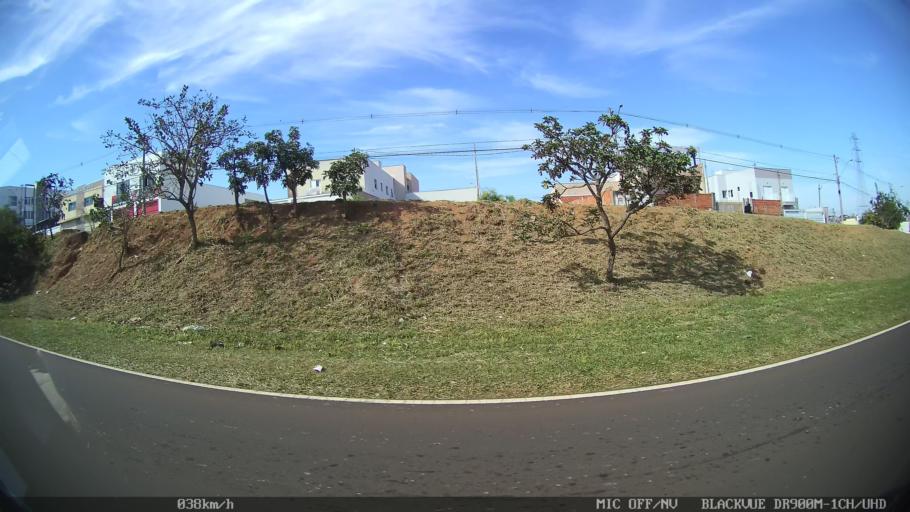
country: BR
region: Sao Paulo
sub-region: Franca
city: Franca
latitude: -20.5140
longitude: -47.4398
